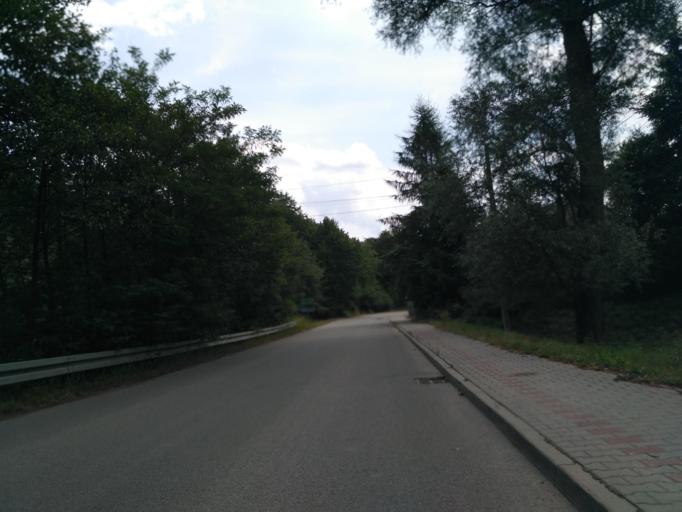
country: PL
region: Subcarpathian Voivodeship
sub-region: Powiat ropczycko-sedziszowski
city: Niedzwiada
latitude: 50.0413
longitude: 21.4966
